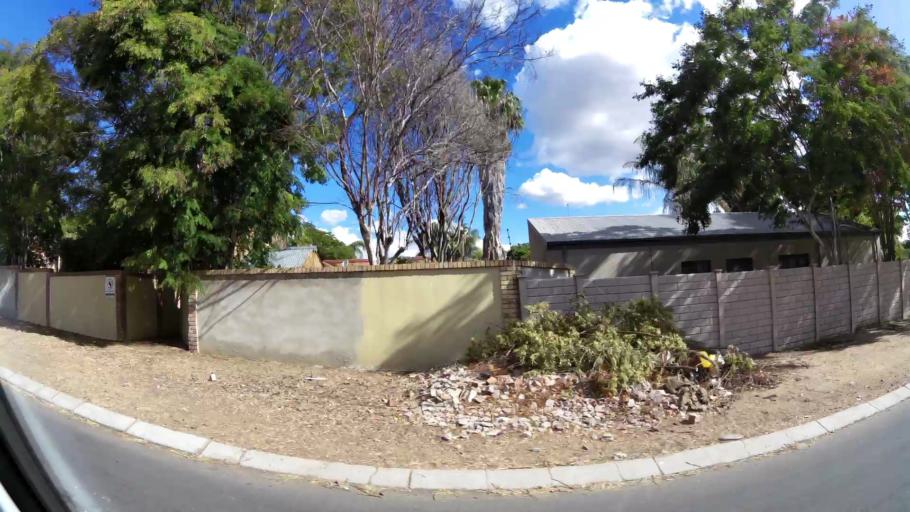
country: ZA
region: Limpopo
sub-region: Capricorn District Municipality
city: Polokwane
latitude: -23.8815
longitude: 29.4705
